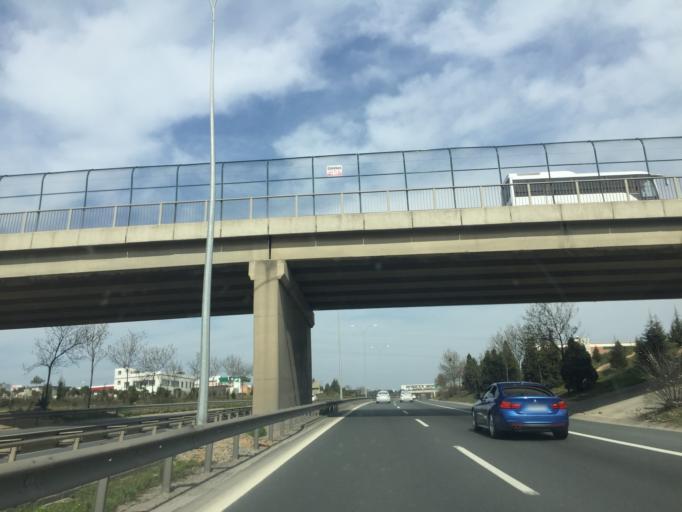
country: TR
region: Kocaeli
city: Balcik
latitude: 40.8574
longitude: 29.3770
